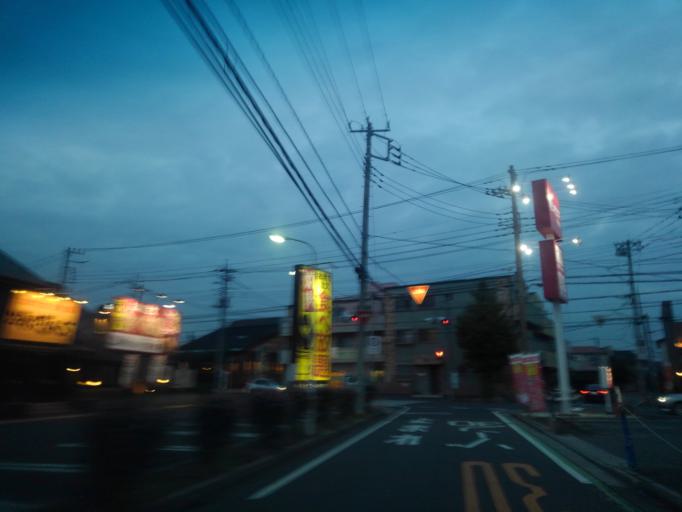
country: JP
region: Saitama
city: Tokorozawa
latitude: 35.8022
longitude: 139.4449
